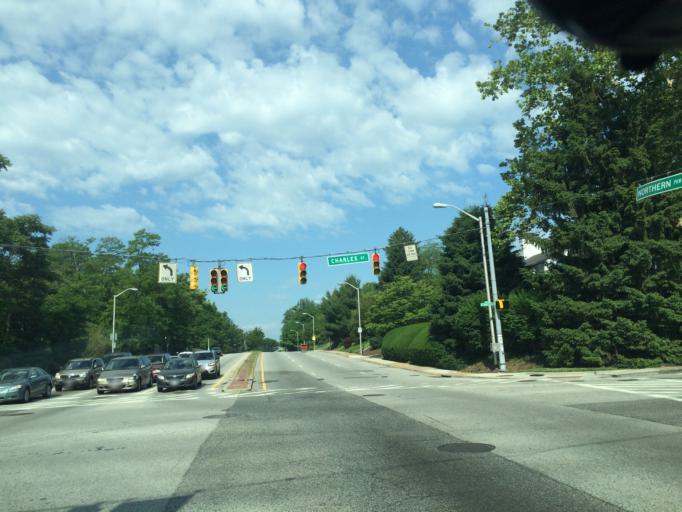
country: US
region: Maryland
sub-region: Baltimore County
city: Towson
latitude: 39.3621
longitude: -76.6248
